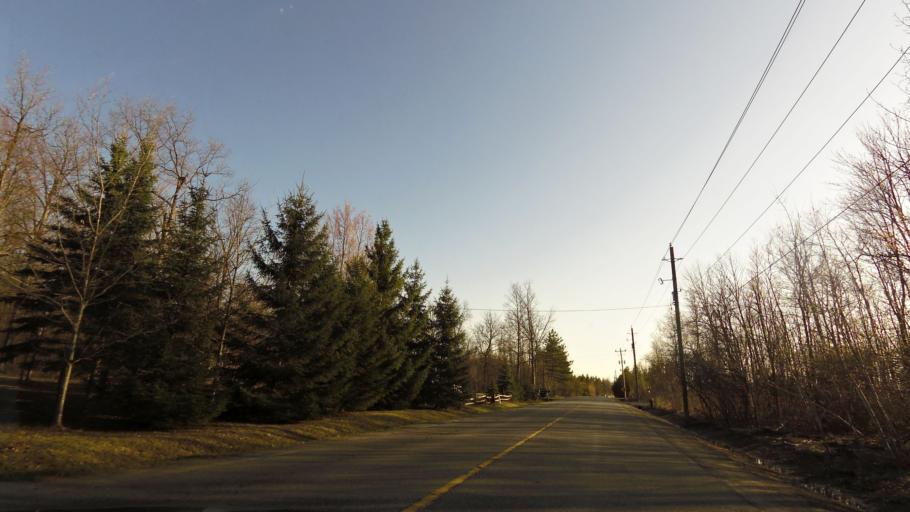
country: CA
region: Ontario
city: Brampton
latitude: 43.8512
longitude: -79.7411
